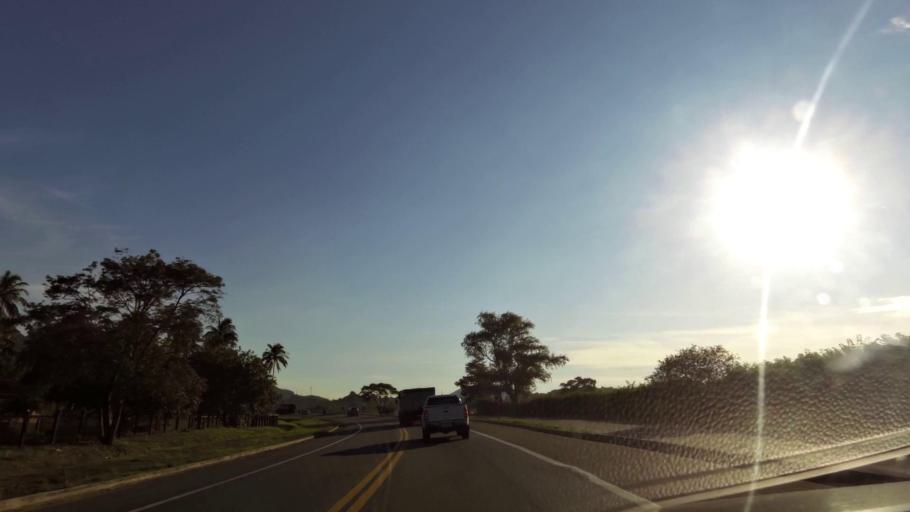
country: BR
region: Espirito Santo
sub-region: Guarapari
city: Guarapari
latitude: -20.6038
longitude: -40.5031
